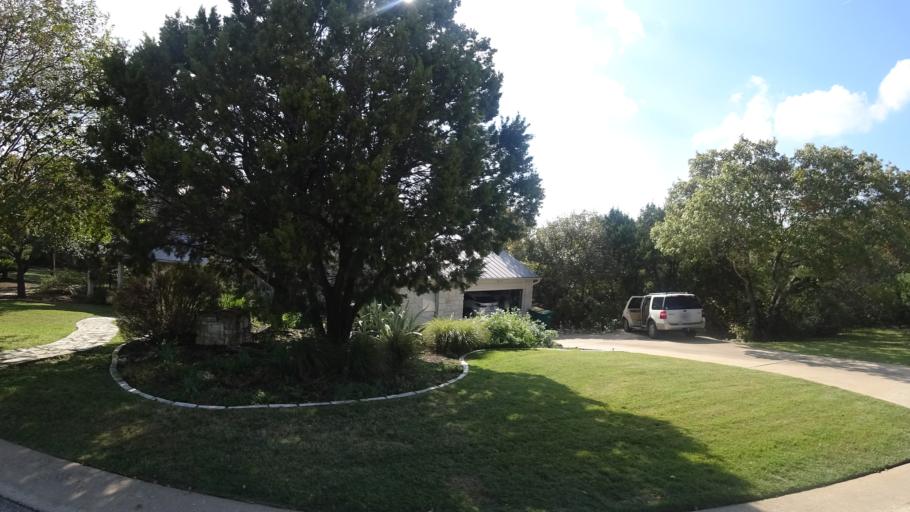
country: US
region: Texas
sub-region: Travis County
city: Lost Creek
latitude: 30.3075
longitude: -97.8541
